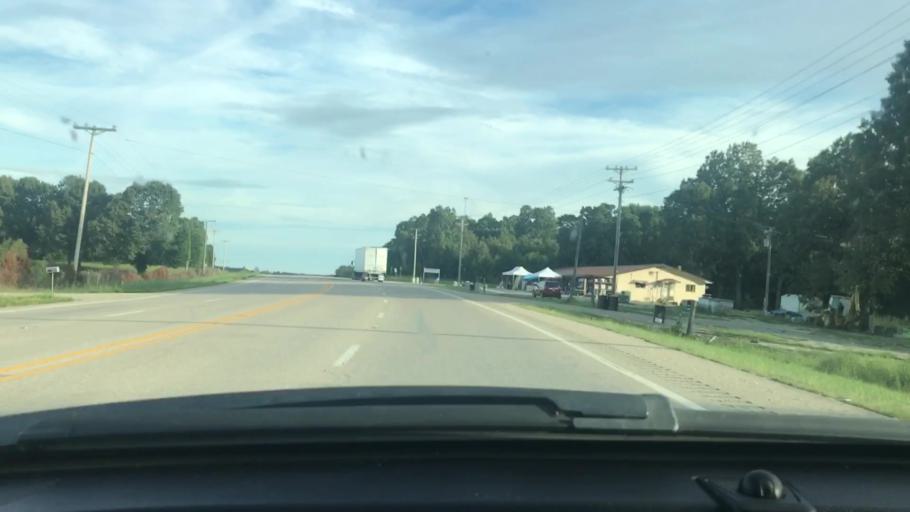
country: US
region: Arkansas
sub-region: Lawrence County
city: Hoxie
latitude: 36.1286
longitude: -91.1575
